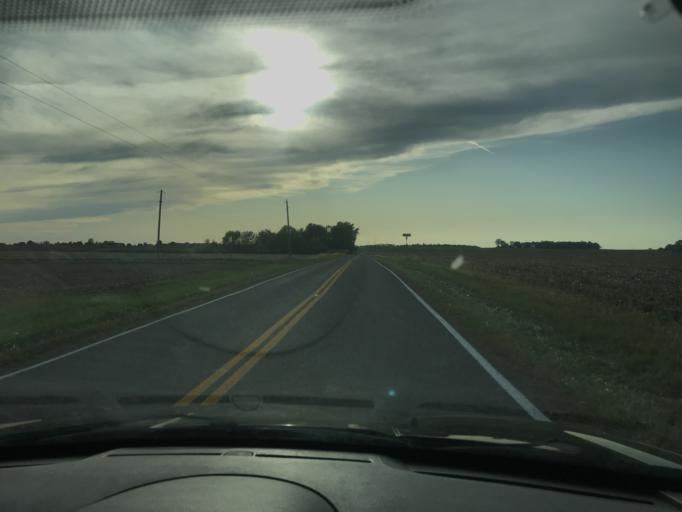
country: US
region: Ohio
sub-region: Logan County
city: West Liberty
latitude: 40.2132
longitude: -83.6903
